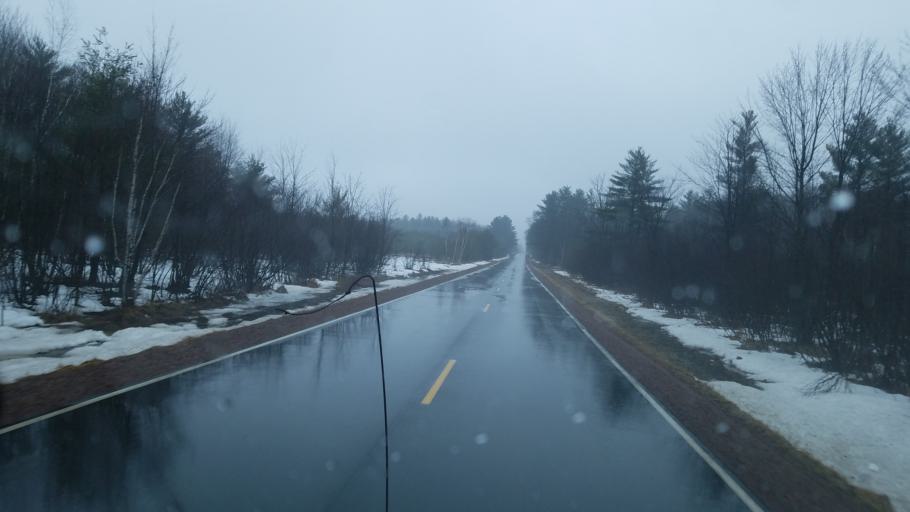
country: US
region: Wisconsin
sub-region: Wood County
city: Marshfield
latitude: 44.5326
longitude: -90.2997
